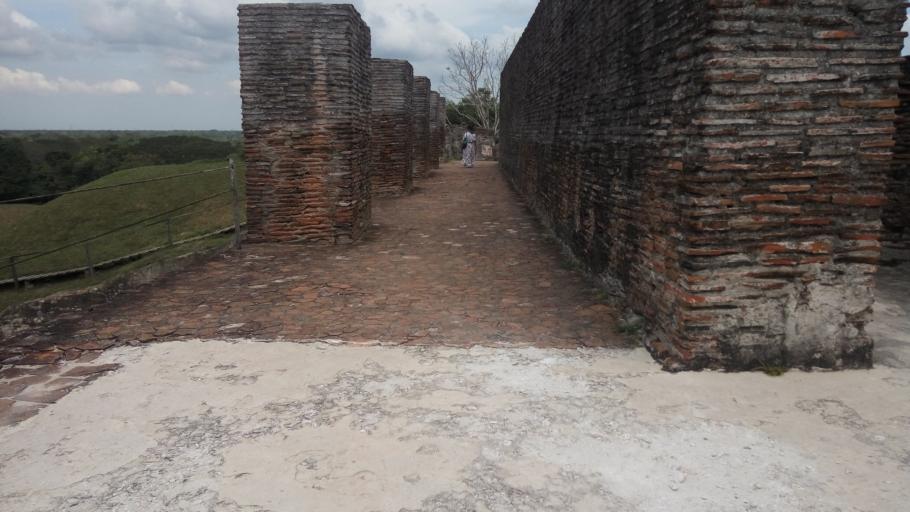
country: MX
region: Tabasco
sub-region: Comalcalco
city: Oriente 1ra. Seccion (Santo Domingo)
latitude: 18.2782
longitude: -93.2004
